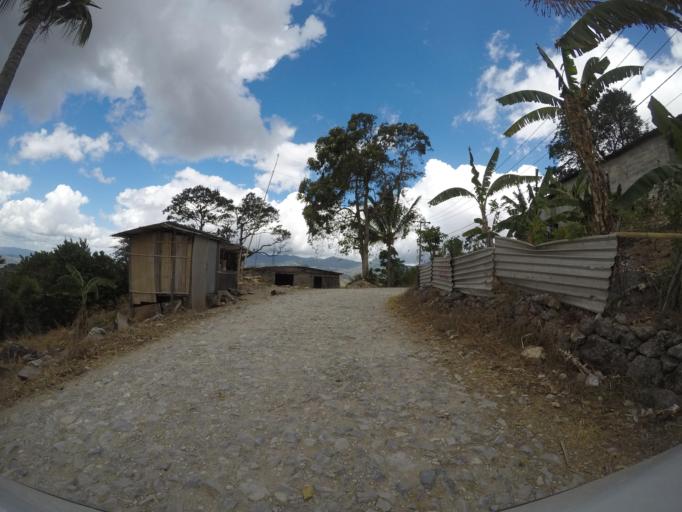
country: TL
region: Baucau
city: Baucau
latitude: -8.5213
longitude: 126.6948
